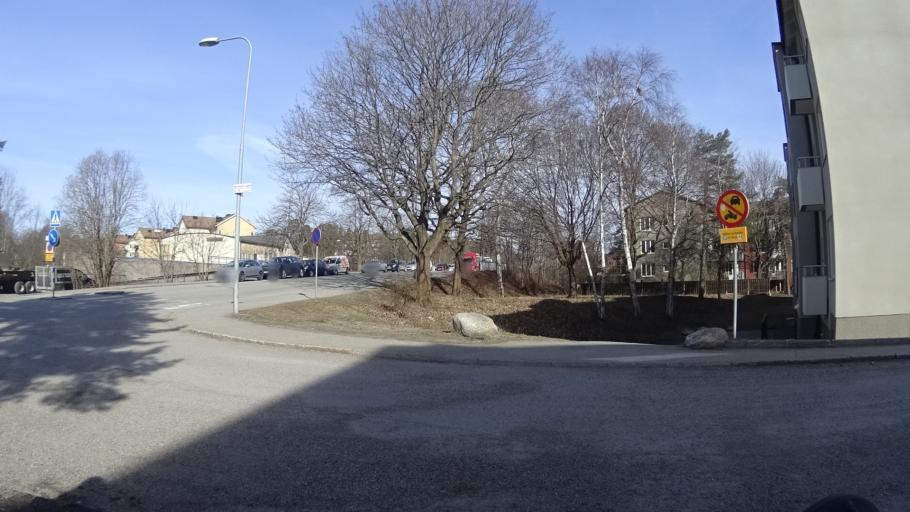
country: SE
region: Stockholm
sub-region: Nacka Kommun
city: Nacka
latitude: 59.2768
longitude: 18.1277
